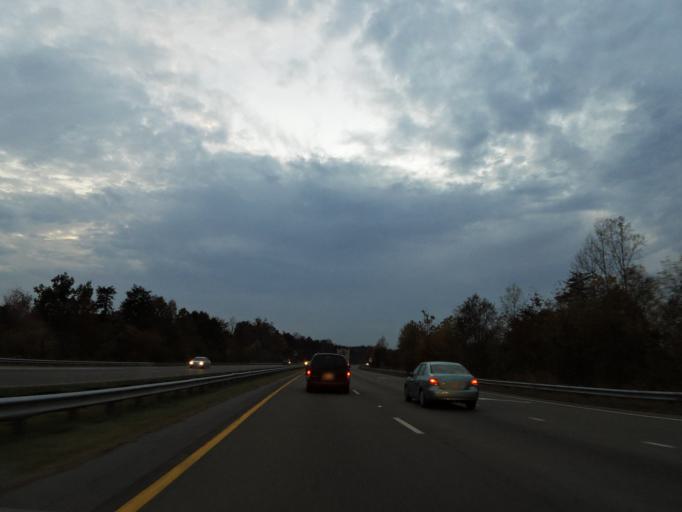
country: US
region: North Carolina
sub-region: Burke County
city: Glen Alpine
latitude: 35.6925
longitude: -81.8134
